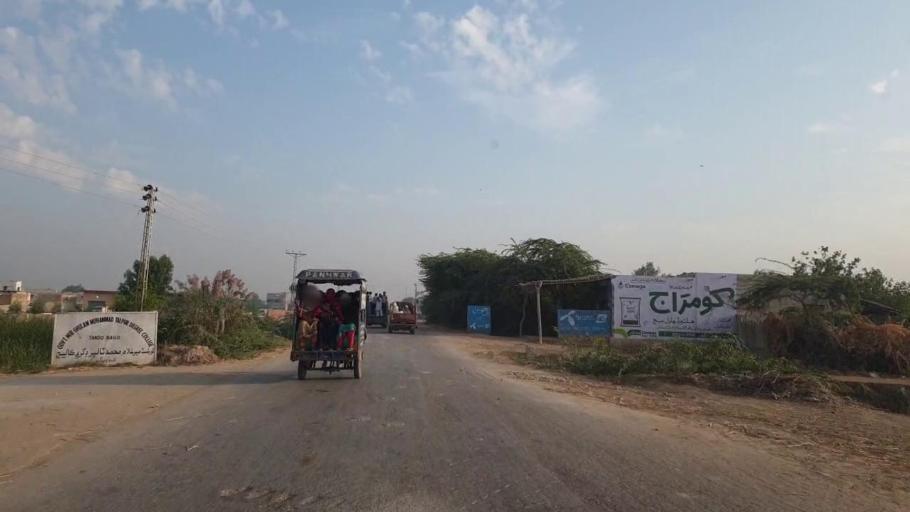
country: PK
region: Sindh
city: Tando Bago
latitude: 24.7759
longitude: 68.9608
